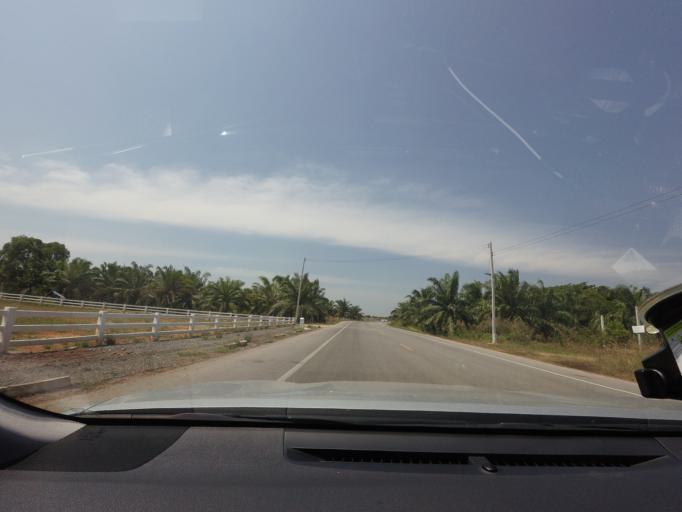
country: TH
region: Surat Thani
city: Tha Chang
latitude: 9.2150
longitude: 99.2048
